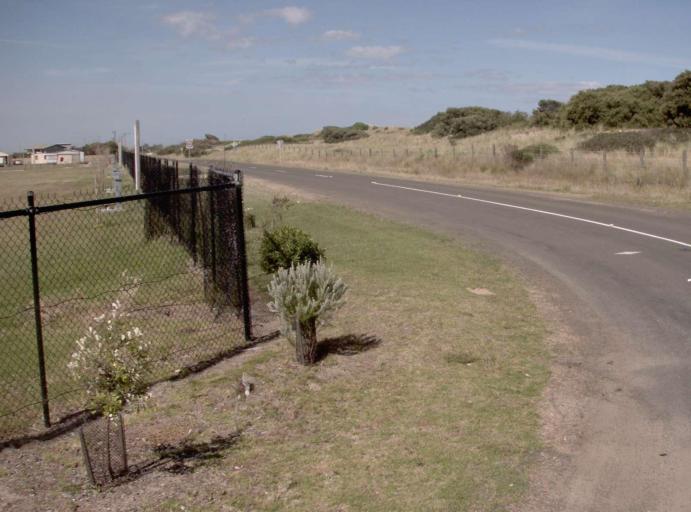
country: AU
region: Victoria
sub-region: Wellington
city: Sale
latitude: -38.3765
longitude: 147.1906
